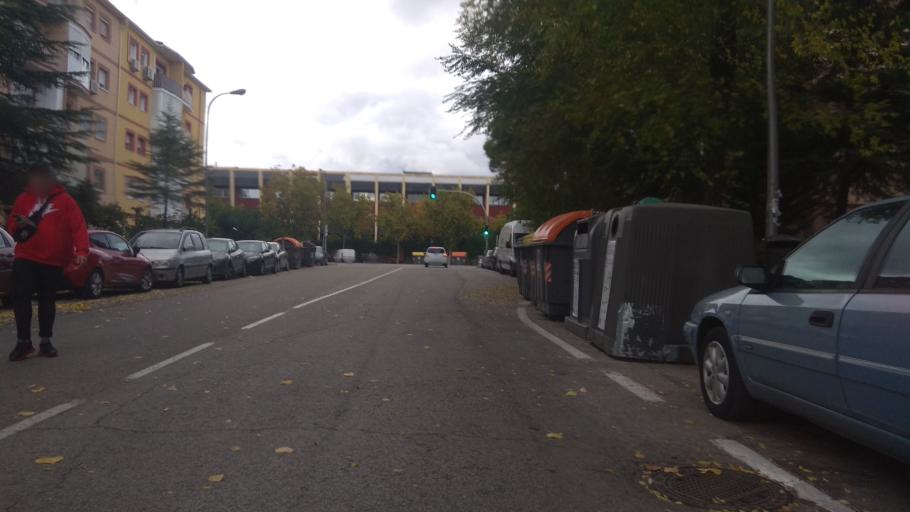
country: ES
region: Madrid
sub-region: Provincia de Madrid
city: Vicalvaro
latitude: 40.4083
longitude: -3.6128
